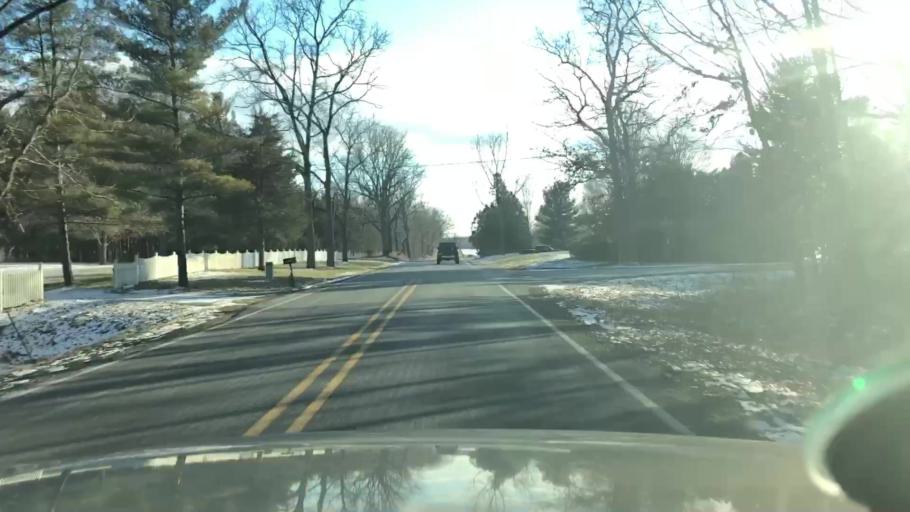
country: US
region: Michigan
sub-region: Jackson County
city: Vandercook Lake
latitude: 42.1054
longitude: -84.4512
